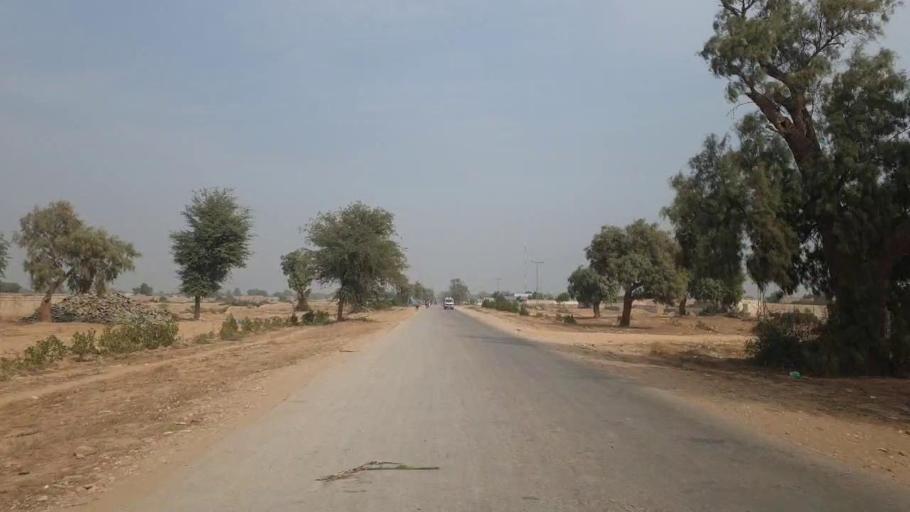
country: PK
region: Sindh
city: Sann
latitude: 26.0321
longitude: 68.1286
